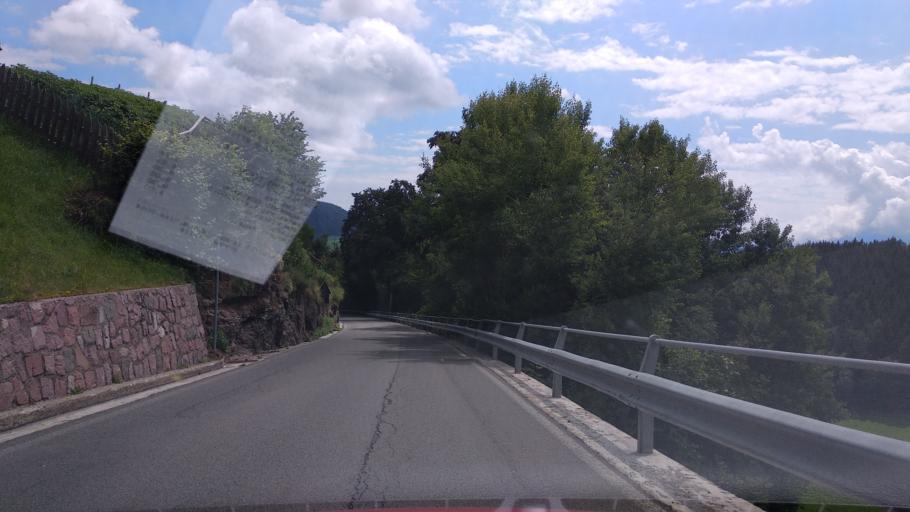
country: IT
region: Trentino-Alto Adige
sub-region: Bolzano
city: Avelengo
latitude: 46.6525
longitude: 11.2191
